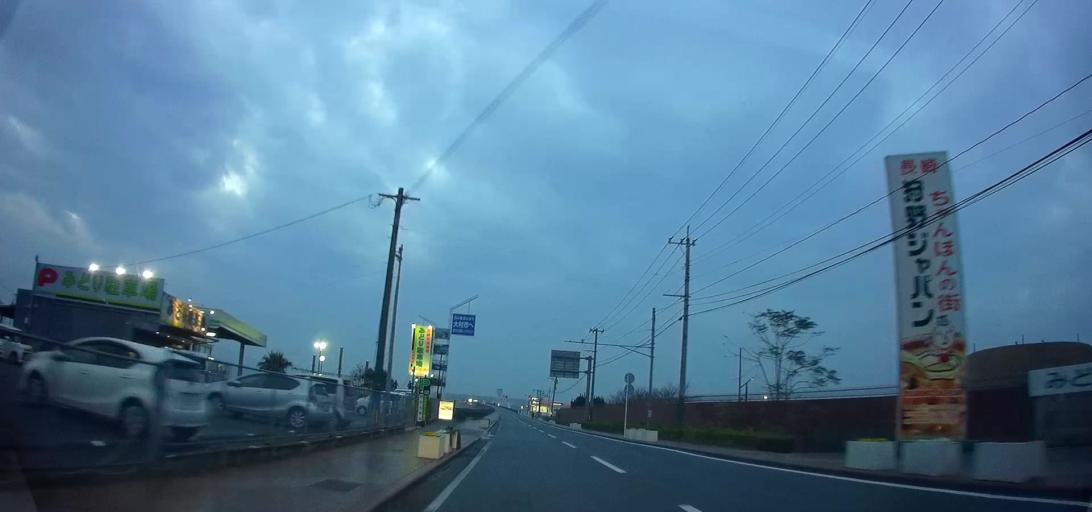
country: JP
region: Nagasaki
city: Omura
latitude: 32.9209
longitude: 129.9376
